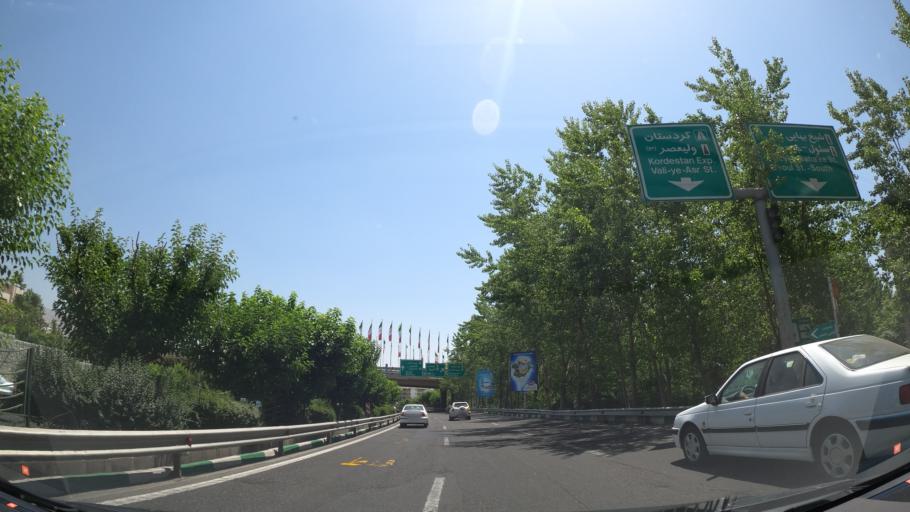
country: IR
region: Tehran
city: Tajrish
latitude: 35.7749
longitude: 51.3943
